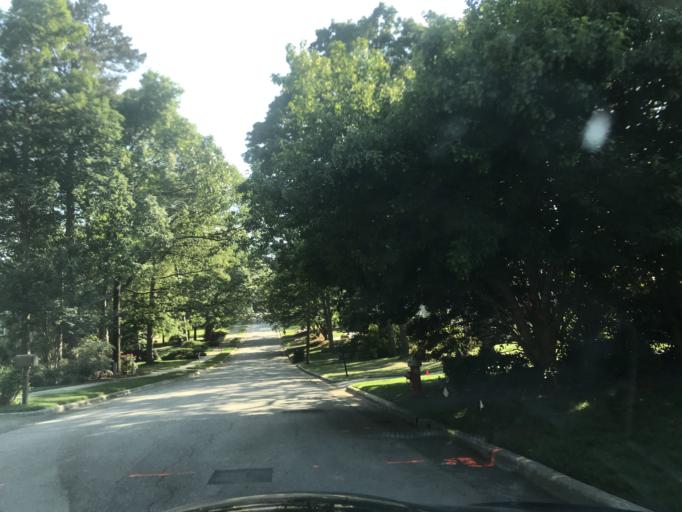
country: US
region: North Carolina
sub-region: Wake County
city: West Raleigh
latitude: 35.8732
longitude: -78.6171
